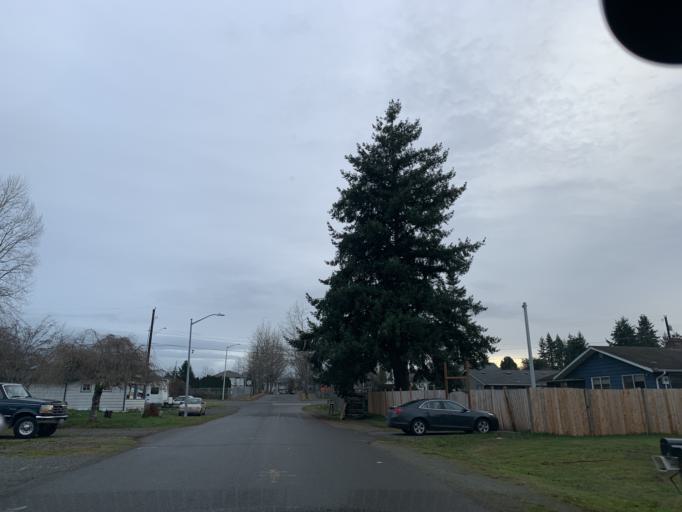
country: US
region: Washington
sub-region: Snohomish County
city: Marysville
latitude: 48.0880
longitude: -122.1633
